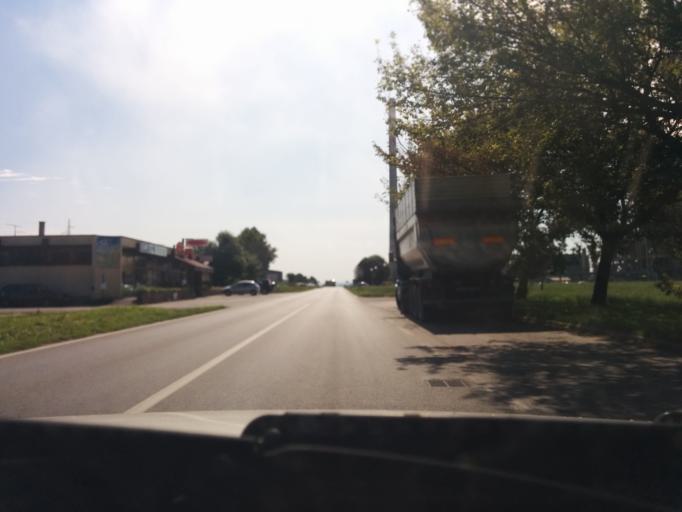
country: HR
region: Sisacko-Moslavacka
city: Kutina
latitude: 45.4712
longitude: 16.7959
